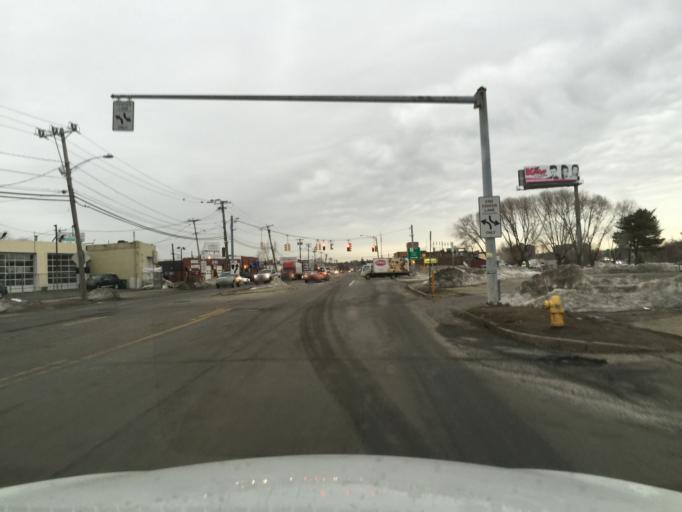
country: US
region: Massachusetts
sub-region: Middlesex County
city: Medford
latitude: 42.4059
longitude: -71.1016
